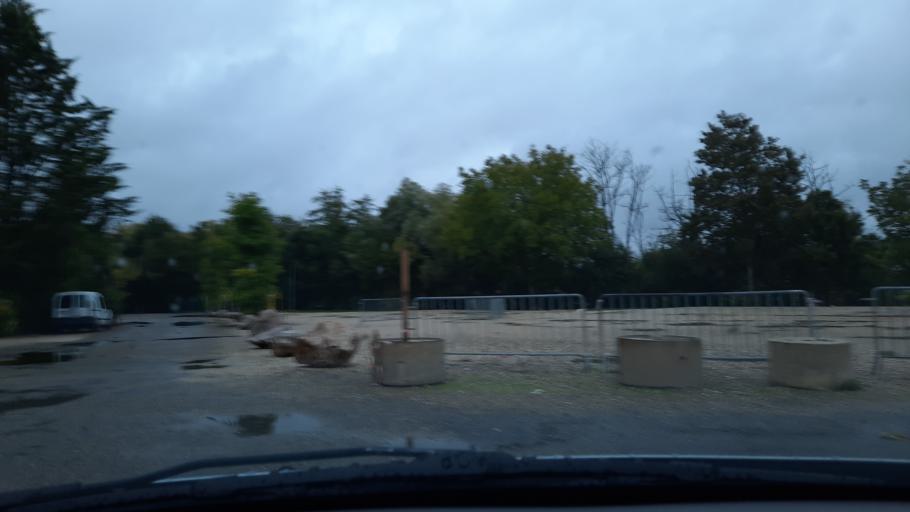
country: FR
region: Midi-Pyrenees
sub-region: Departement du Tarn-et-Garonne
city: Lafrancaise
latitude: 44.1890
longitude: 1.2858
